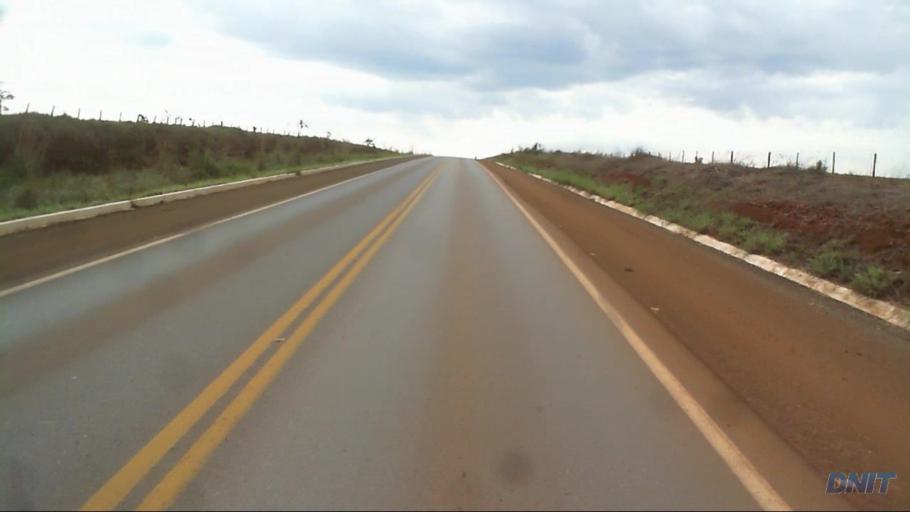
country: BR
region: Goias
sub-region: Uruacu
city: Uruacu
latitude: -14.6904
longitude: -49.1275
